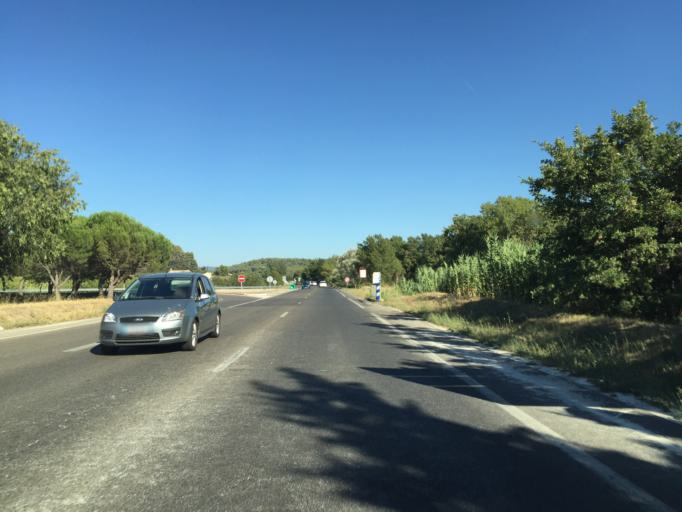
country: FR
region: Provence-Alpes-Cote d'Azur
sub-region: Departement du Vaucluse
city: Menerbes
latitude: 43.8591
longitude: 5.1931
